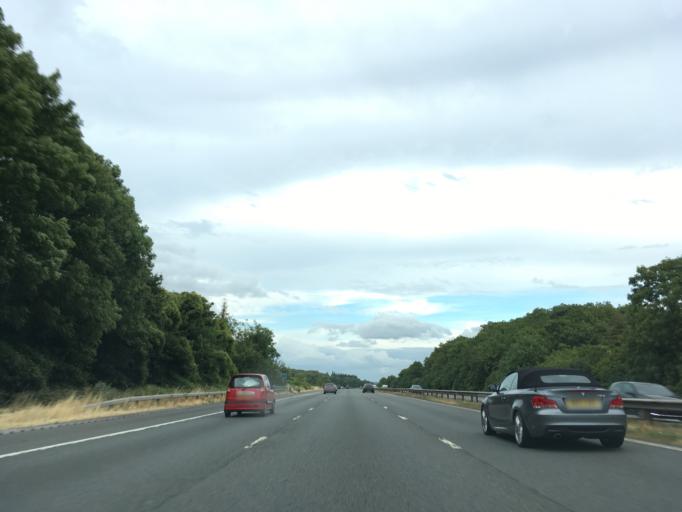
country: GB
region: England
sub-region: South Gloucestershire
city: Tytherington
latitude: 51.5961
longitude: -2.4866
